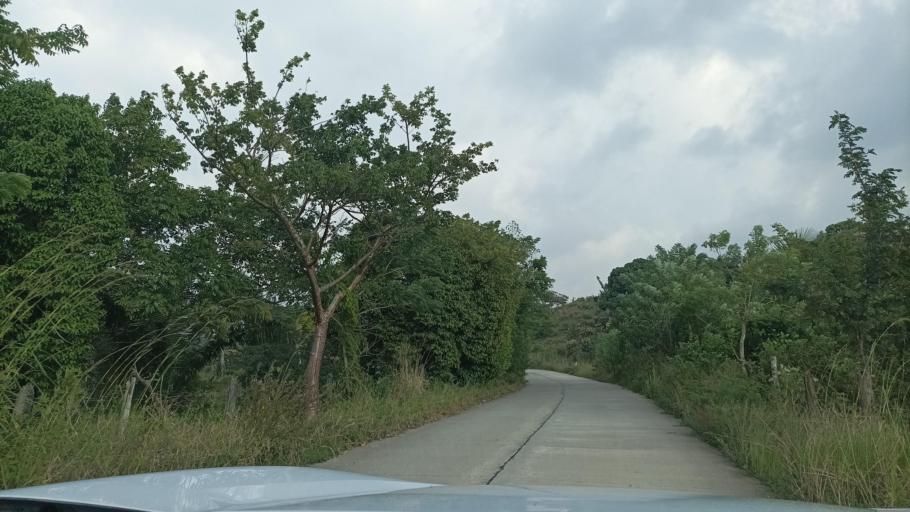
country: MX
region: Veracruz
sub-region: Moloacan
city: Tlacuilolapan
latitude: 18.0761
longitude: -94.2896
